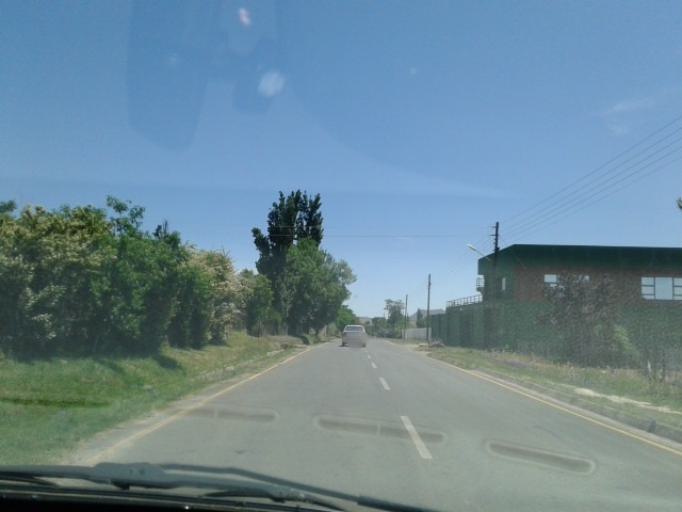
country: LS
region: Maseru
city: Maseru
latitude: -29.3025
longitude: 27.4770
